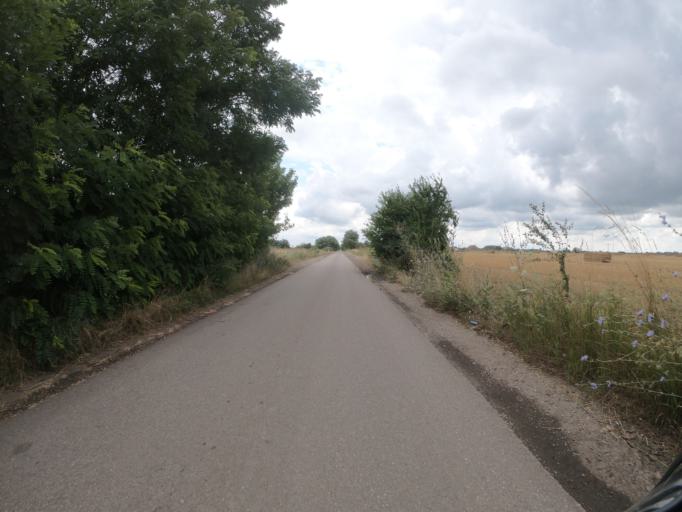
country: HU
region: Borsod-Abauj-Zemplen
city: Szentistvan
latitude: 47.7115
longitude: 20.6954
